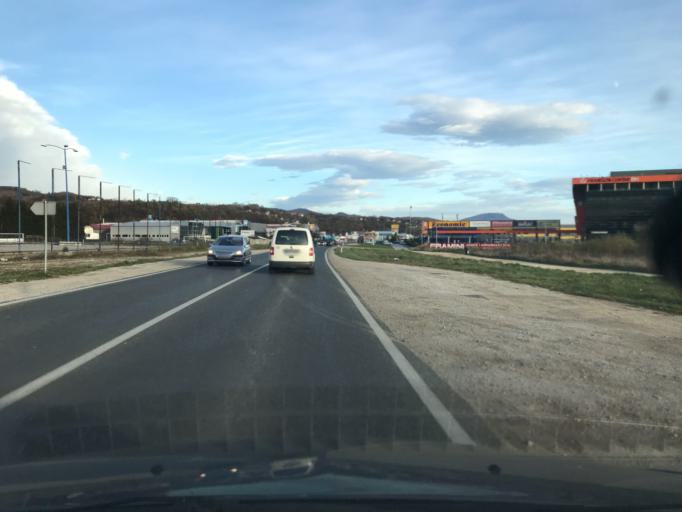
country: BA
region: Federation of Bosnia and Herzegovina
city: Vitez
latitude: 44.1702
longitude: 17.7765
